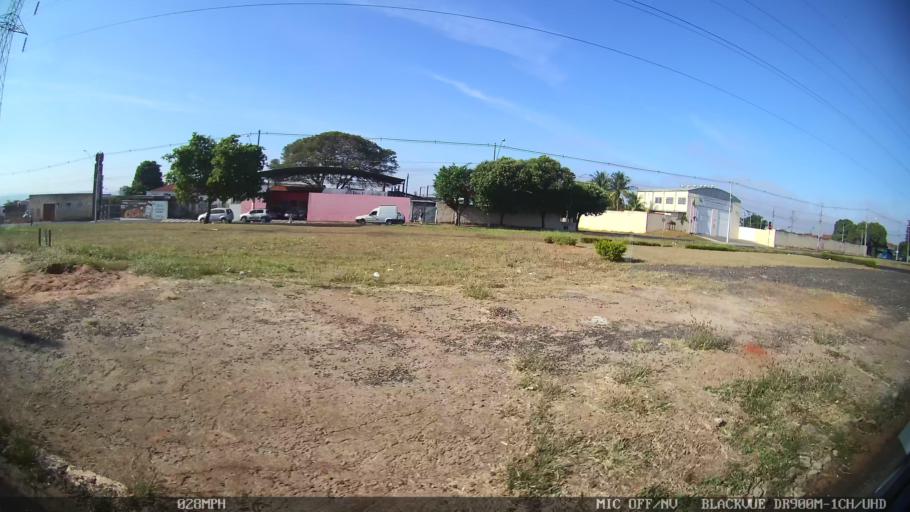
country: BR
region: Sao Paulo
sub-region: Sao Jose Do Rio Preto
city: Sao Jose do Rio Preto
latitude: -20.7800
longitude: -49.4045
